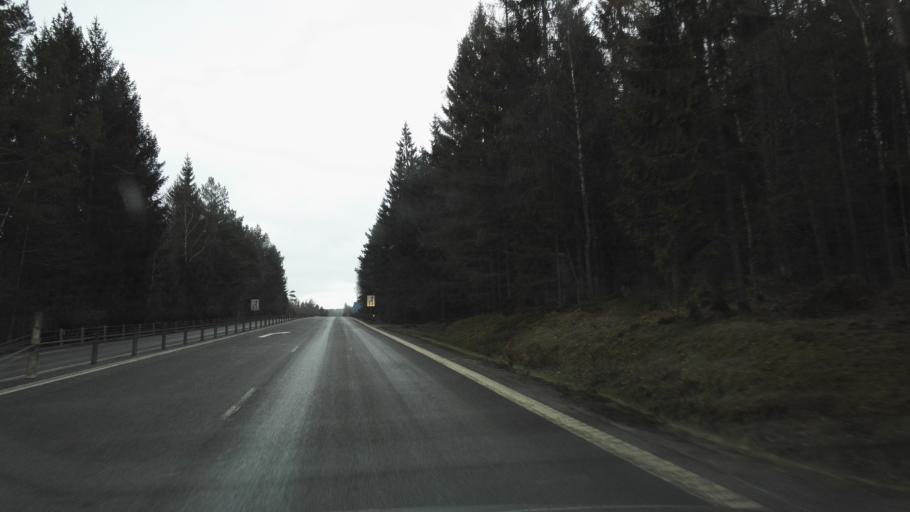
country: SE
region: Skane
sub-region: Ostra Goinge Kommun
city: Broby
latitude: 56.2827
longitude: 14.0151
